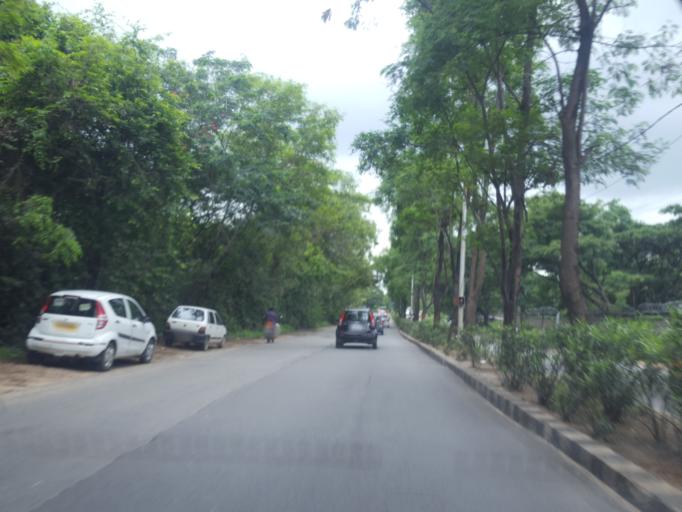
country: IN
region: Telangana
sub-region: Medak
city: Serilingampalle
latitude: 17.4555
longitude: 78.3411
